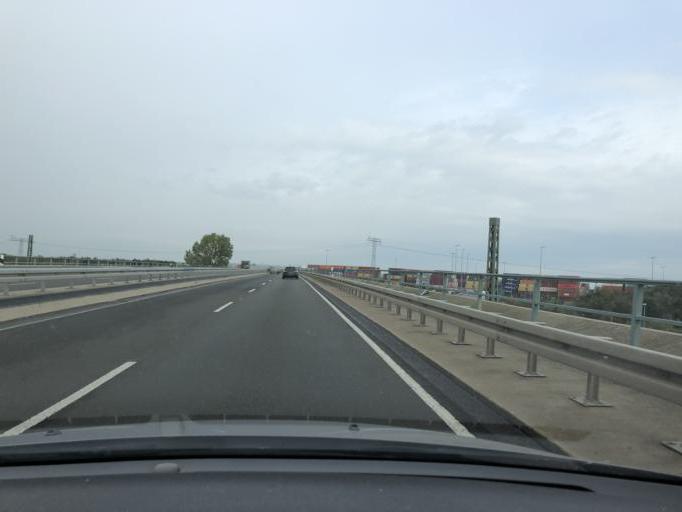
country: DE
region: Saxony
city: Schkeuditz
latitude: 51.3890
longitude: 12.2958
